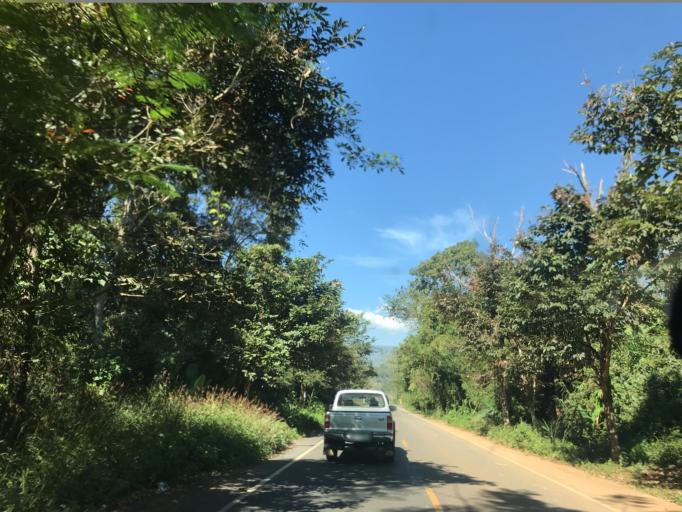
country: TH
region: Chiang Rai
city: Mae Lao
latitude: 19.8068
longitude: 99.6473
